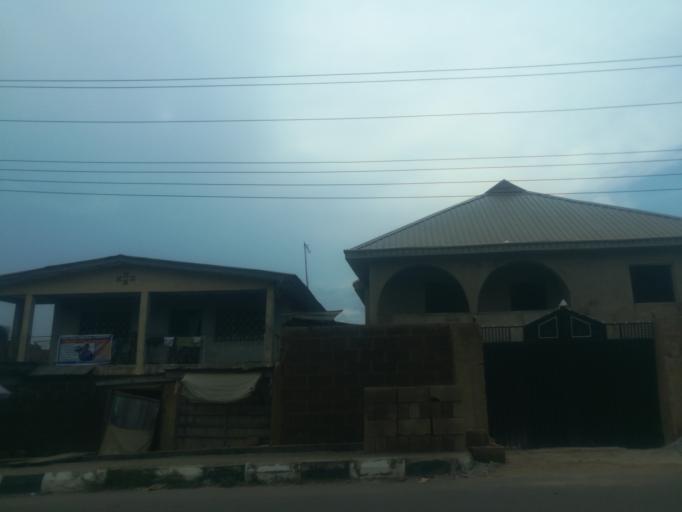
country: NG
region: Oyo
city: Ibadan
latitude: 7.3806
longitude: 3.8289
